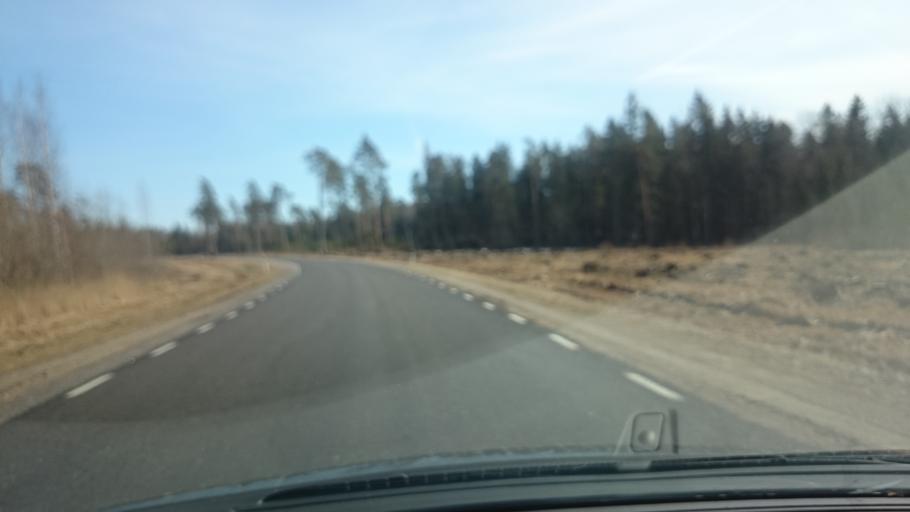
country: EE
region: Paernumaa
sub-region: Tootsi vald
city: Tootsi
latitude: 58.6414
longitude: 24.8916
